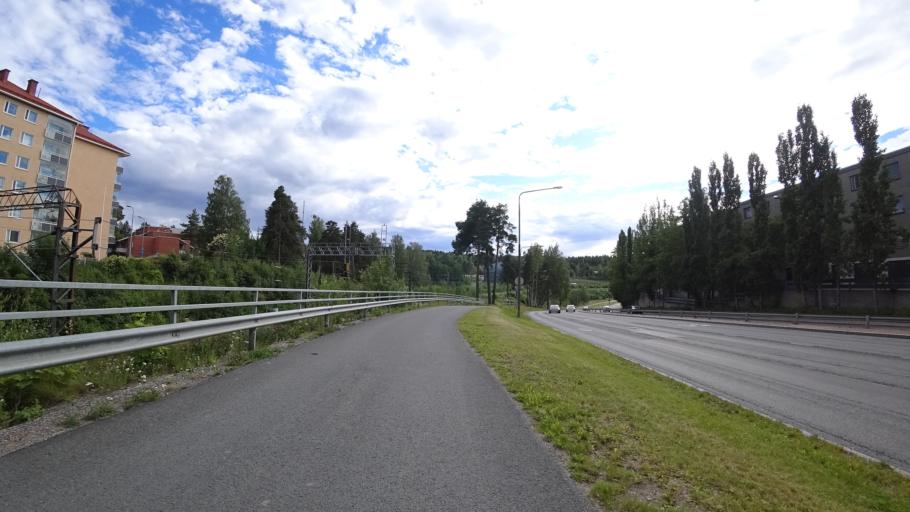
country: FI
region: Pirkanmaa
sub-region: Tampere
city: Tampere
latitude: 61.5012
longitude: 23.7356
